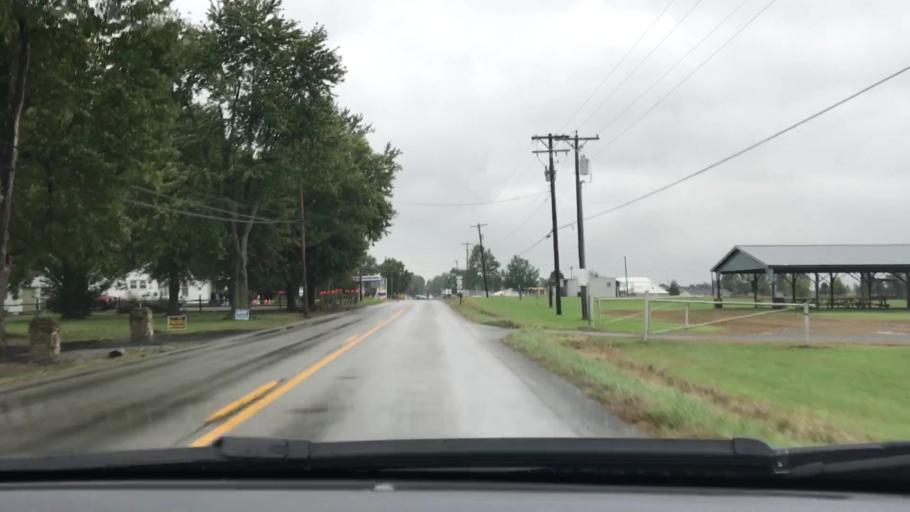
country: US
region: Kentucky
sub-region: McLean County
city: Calhoun
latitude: 37.4083
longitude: -87.2627
